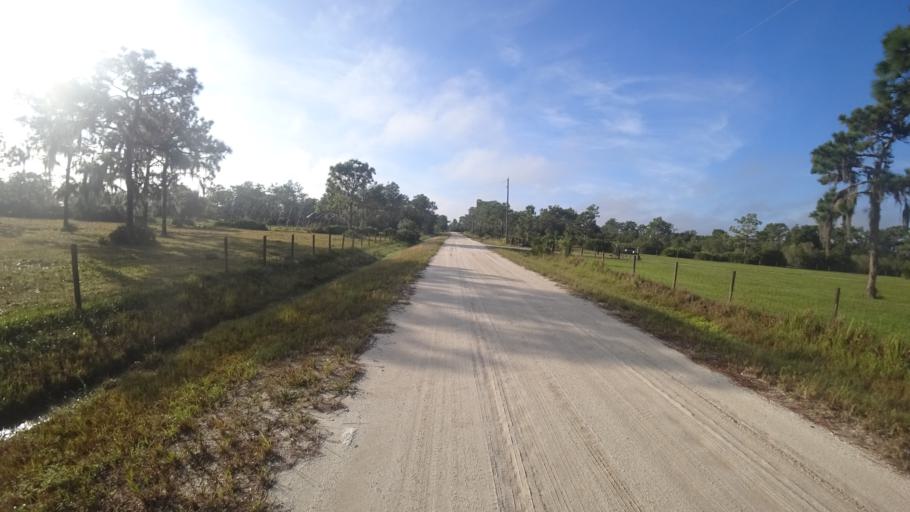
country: US
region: Florida
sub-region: Sarasota County
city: The Meadows
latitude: 27.4076
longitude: -82.2916
